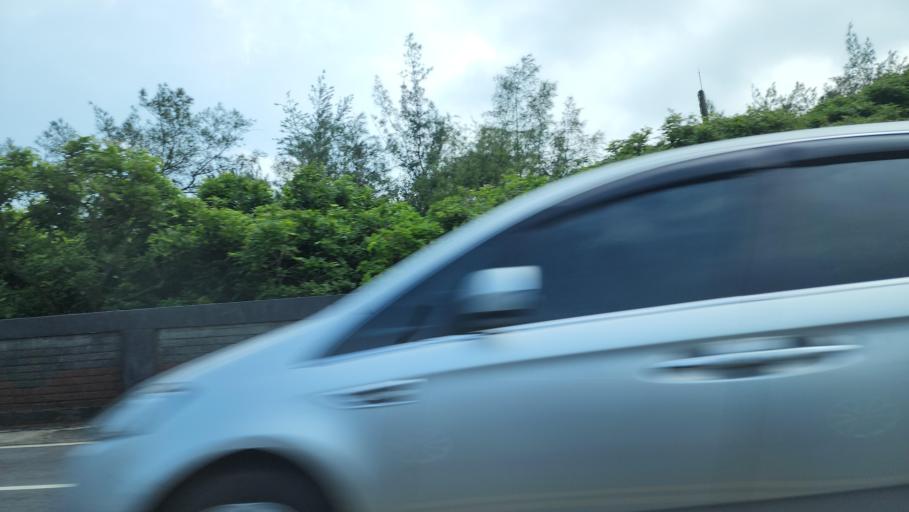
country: TW
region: Taiwan
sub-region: Keelung
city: Keelung
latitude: 25.2279
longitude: 121.6416
